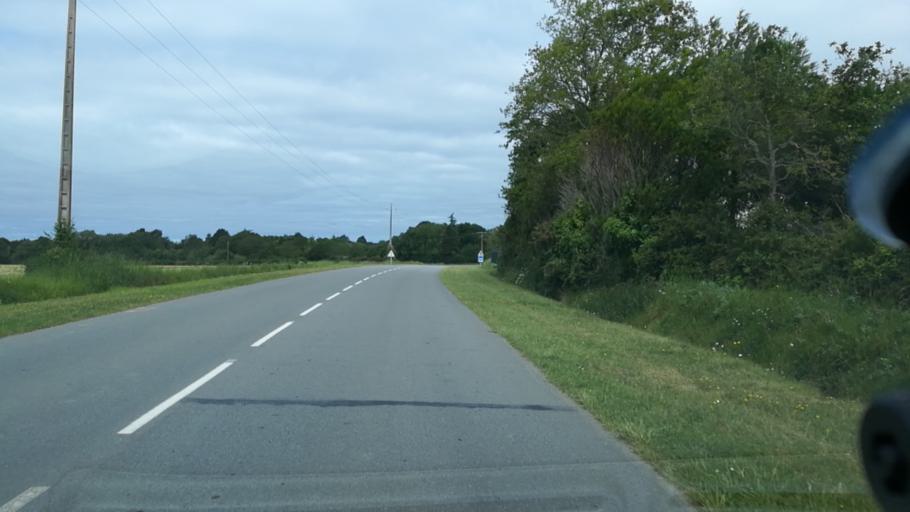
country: FR
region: Brittany
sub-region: Departement du Morbihan
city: Penestin
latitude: 47.4563
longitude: -2.4709
